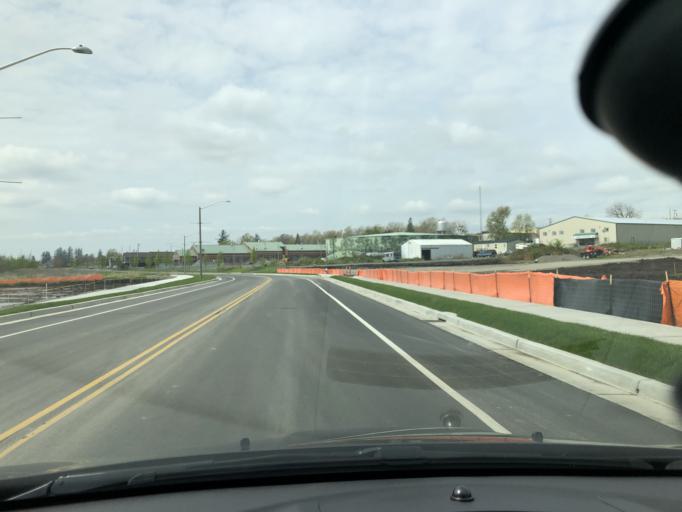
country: US
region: Washington
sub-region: Whatcom County
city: Lynden
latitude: 48.9410
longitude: -122.4497
